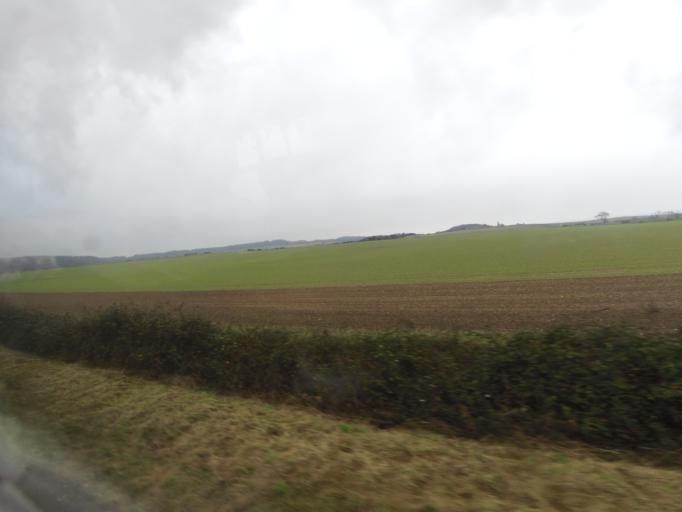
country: GB
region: England
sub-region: Norfolk
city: Sheringham
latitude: 52.9385
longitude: 1.1595
